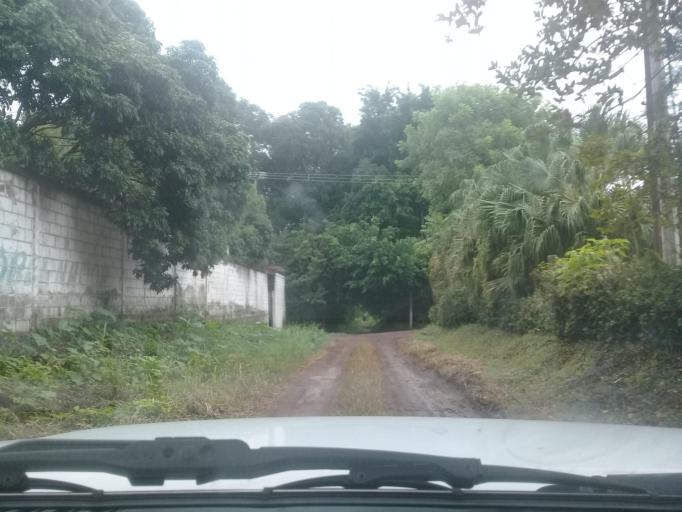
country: MX
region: Veracruz
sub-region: San Andres Tuxtla
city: Cerro las Iguanas
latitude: 18.4262
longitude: -95.1950
